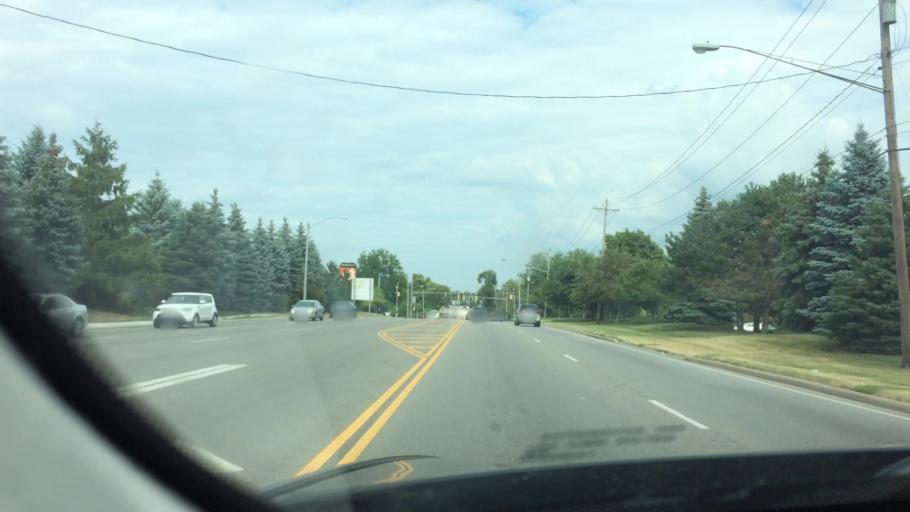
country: US
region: Ohio
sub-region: Lucas County
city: Holland
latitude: 41.6140
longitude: -83.6826
